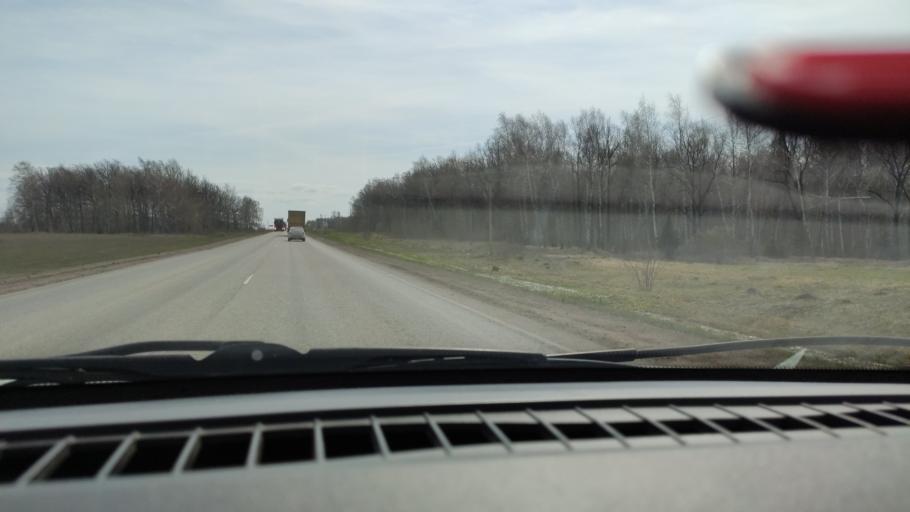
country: RU
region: Bashkortostan
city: Dyurtyuli
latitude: 55.3583
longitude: 54.9032
